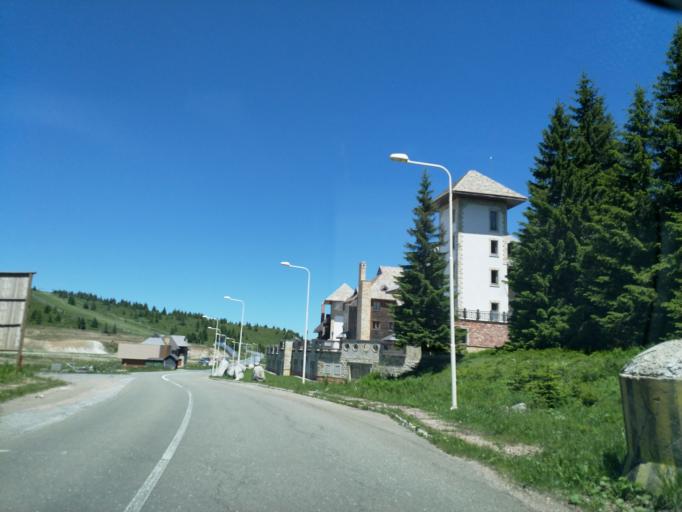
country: XK
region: Mitrovica
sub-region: Komuna e Leposaviqit
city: Leposaviq
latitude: 43.3028
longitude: 20.8248
